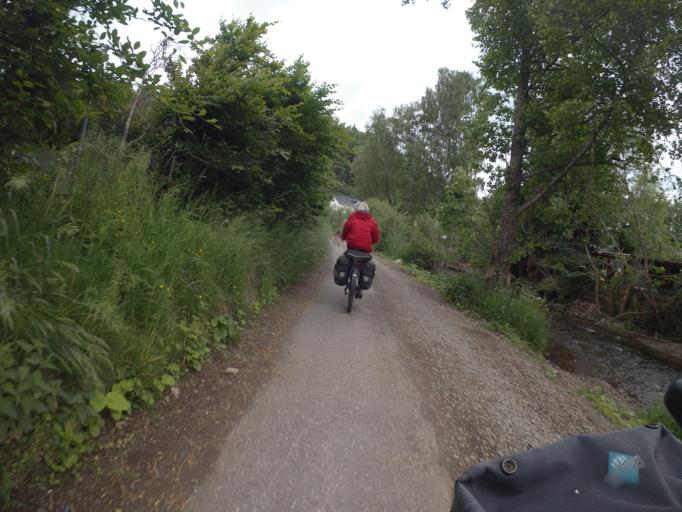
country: DE
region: North Rhine-Westphalia
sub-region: Regierungsbezirk Koln
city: Schleiden
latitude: 50.5083
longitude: 6.4637
